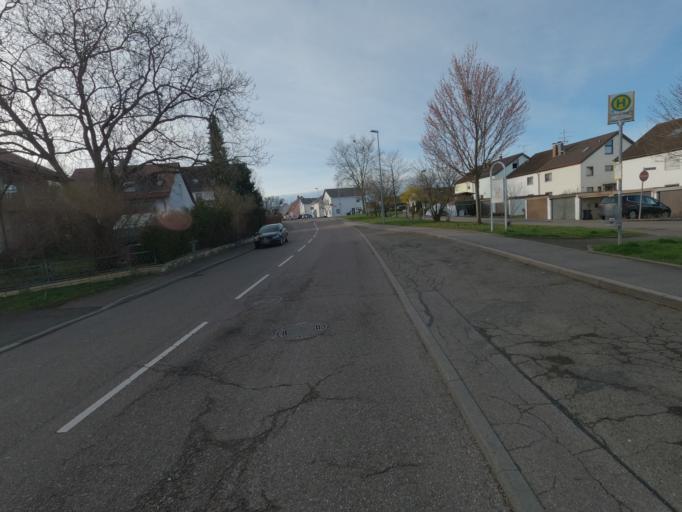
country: DE
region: Baden-Wuerttemberg
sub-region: Regierungsbezirk Stuttgart
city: Uhingen
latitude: 48.6884
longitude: 9.5821
